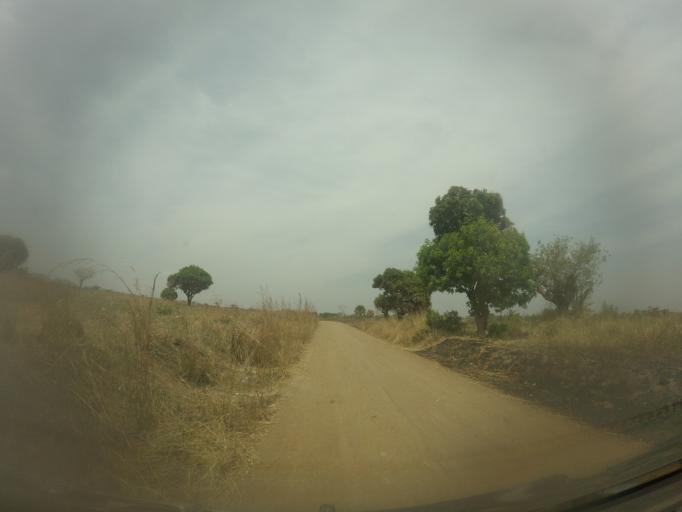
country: UG
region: Northern Region
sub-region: Zombo District
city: Zombo
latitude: 2.7658
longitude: 31.0343
